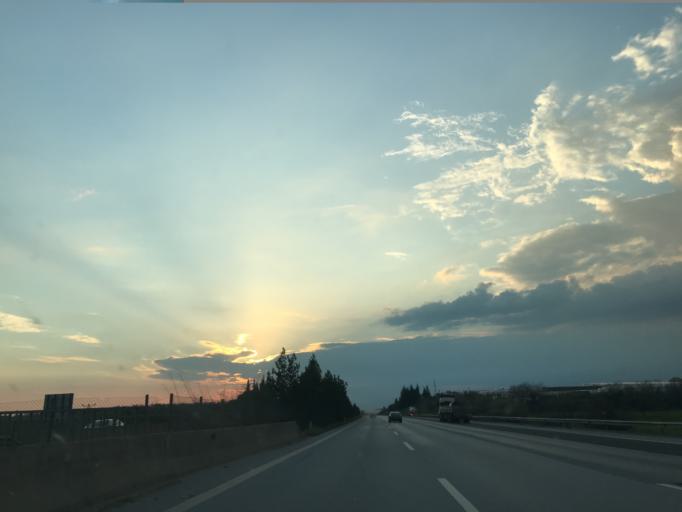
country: TR
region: Mersin
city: Yenice
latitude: 37.0236
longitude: 35.0561
